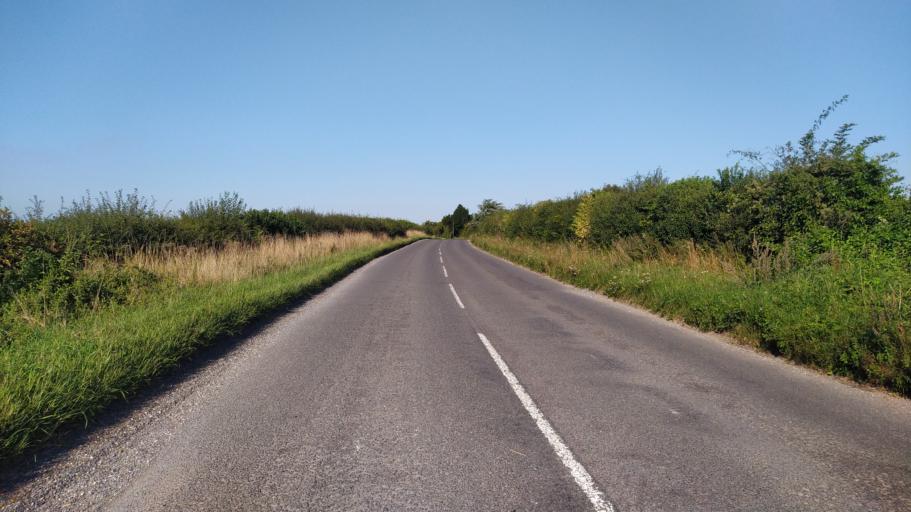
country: GB
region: England
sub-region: Hampshire
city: Abbotts Ann
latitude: 51.1618
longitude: -1.5755
